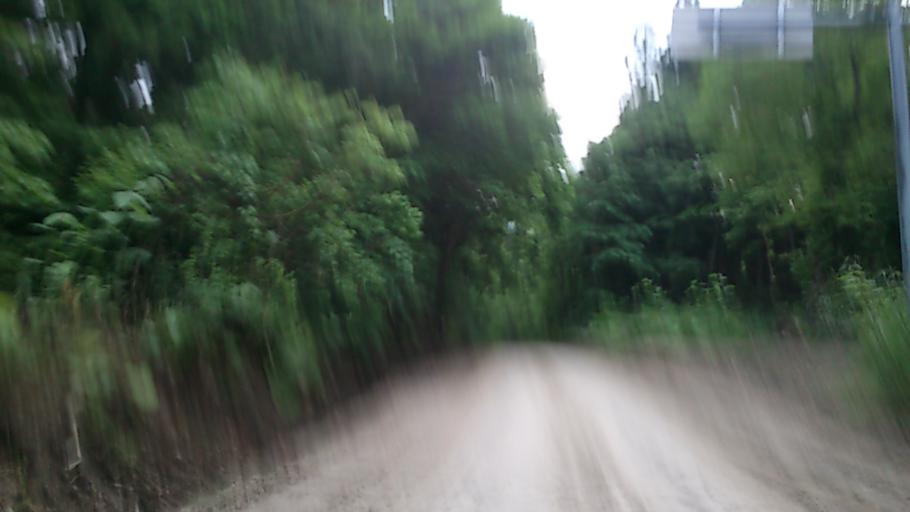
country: JP
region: Aomori
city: Hirosaki
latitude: 40.5335
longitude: 140.1834
